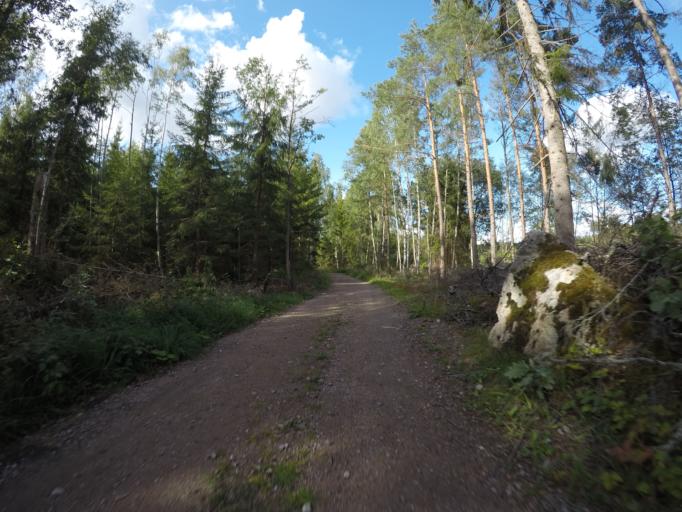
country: SE
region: Soedermanland
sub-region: Eskilstuna Kommun
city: Kvicksund
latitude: 59.5330
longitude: 16.3346
